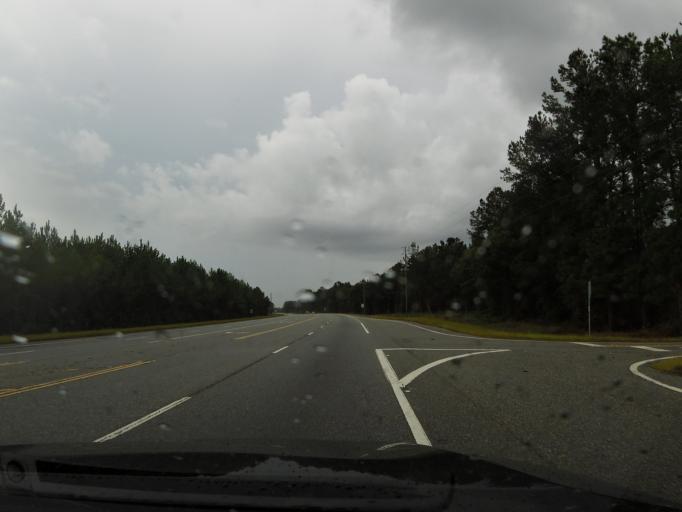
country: US
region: Georgia
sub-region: Wayne County
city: Jesup
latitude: 31.5524
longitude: -81.8149
